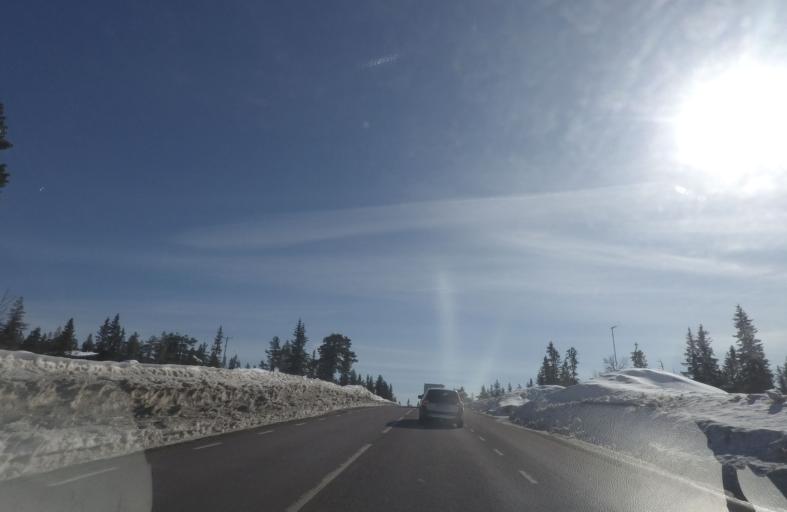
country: SE
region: Dalarna
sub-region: Malung-Saelens kommun
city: Malung
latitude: 61.1701
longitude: 13.0875
